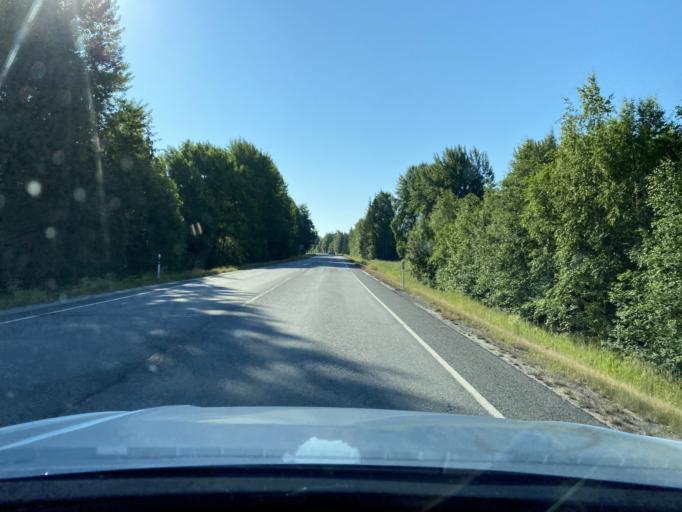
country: FI
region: Haeme
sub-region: Forssa
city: Tammela
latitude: 60.8284
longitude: 23.7337
